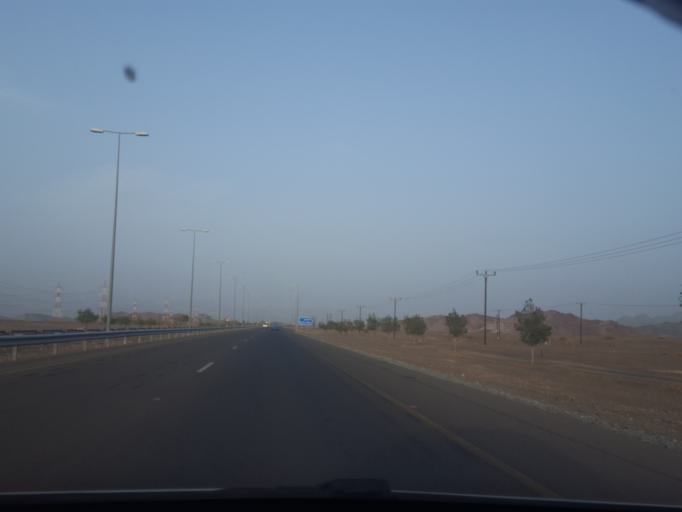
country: OM
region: Al Buraimi
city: Al Buraymi
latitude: 24.2458
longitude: 55.9993
